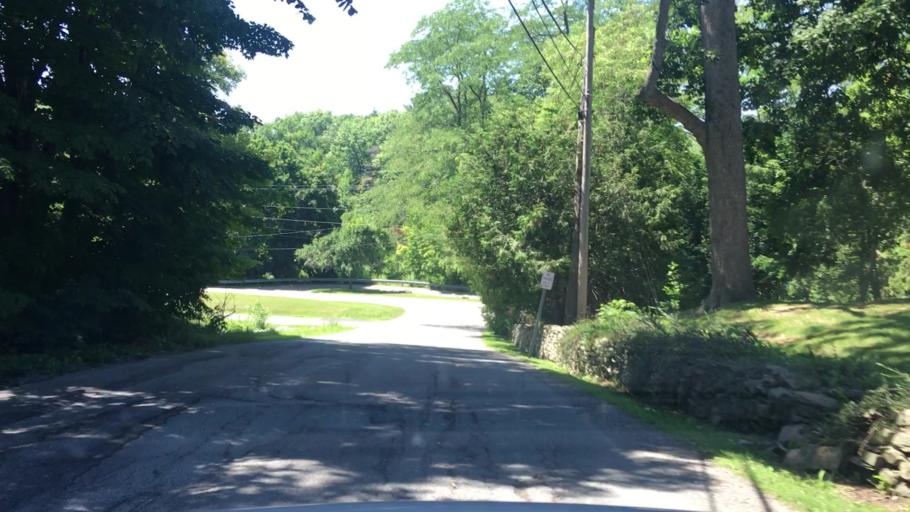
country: US
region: Maine
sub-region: Penobscot County
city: Bangor
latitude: 44.8164
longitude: -68.7890
